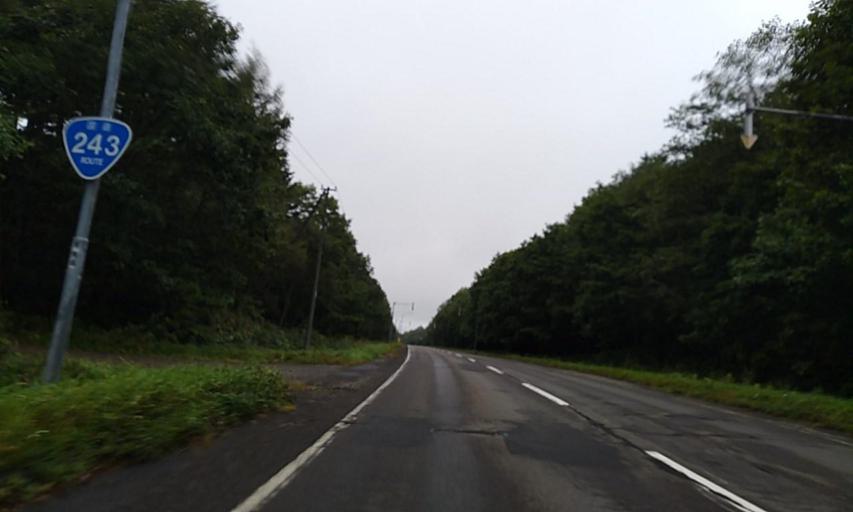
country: JP
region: Hokkaido
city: Kushiro
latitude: 43.4822
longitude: 144.5522
